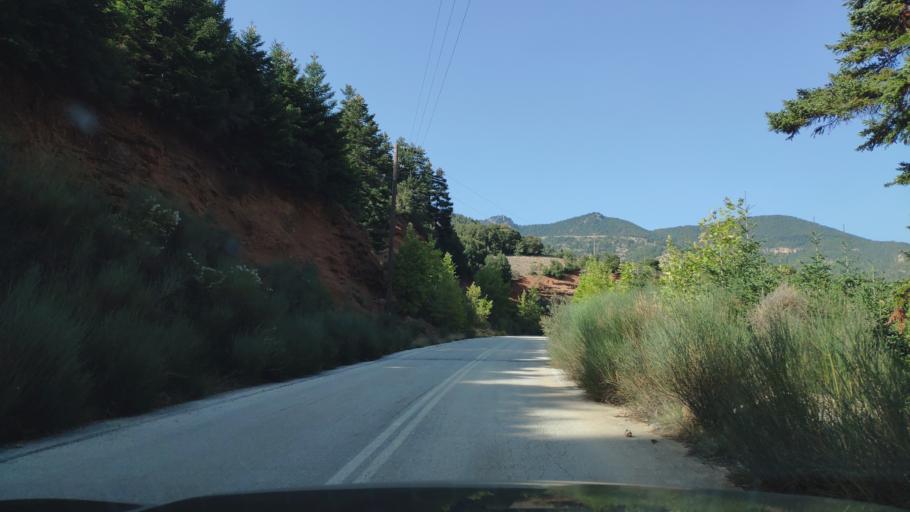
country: GR
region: West Greece
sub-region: Nomos Achaias
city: Aiyira
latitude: 37.9786
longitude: 22.3537
